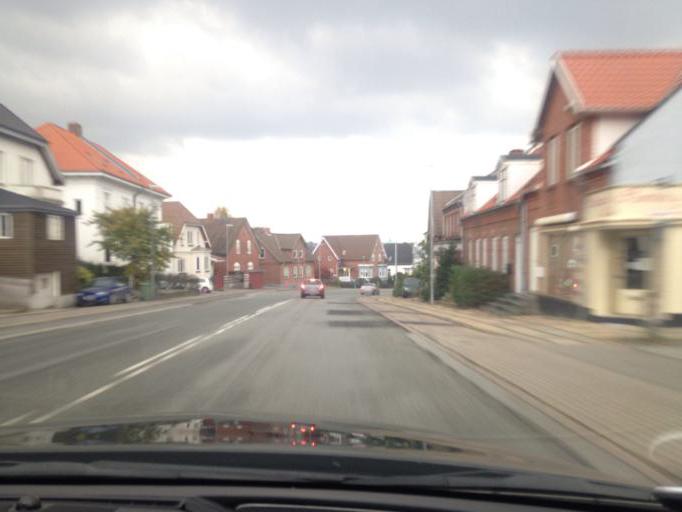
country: DK
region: South Denmark
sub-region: Kolding Kommune
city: Kolding
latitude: 55.4805
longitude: 9.4685
